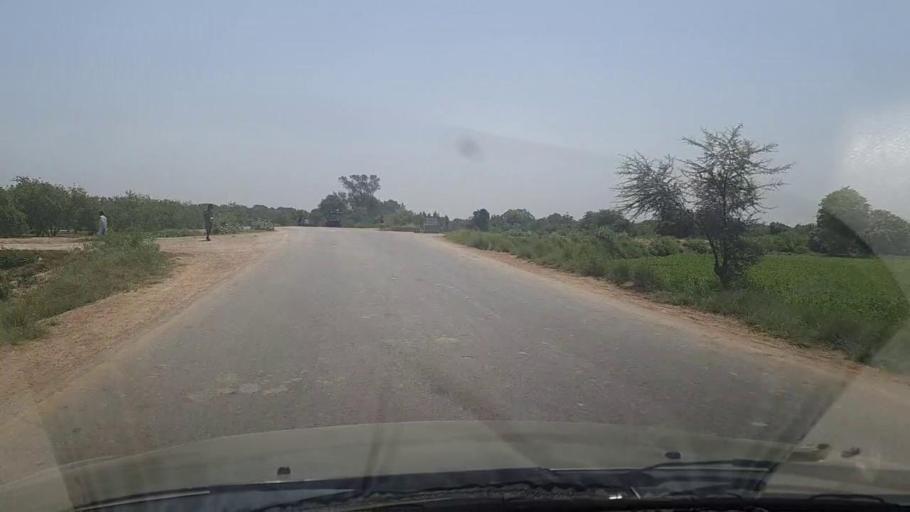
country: PK
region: Sindh
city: Tando Jam
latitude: 25.3539
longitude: 68.5040
